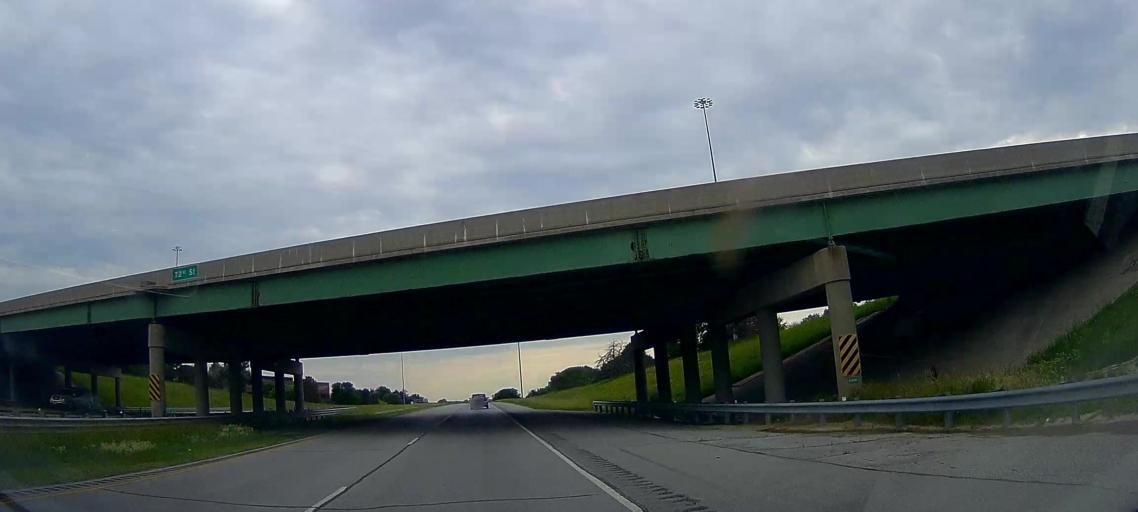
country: US
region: Iowa
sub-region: Pottawattamie County
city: Carter Lake
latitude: 41.3414
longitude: -96.0242
